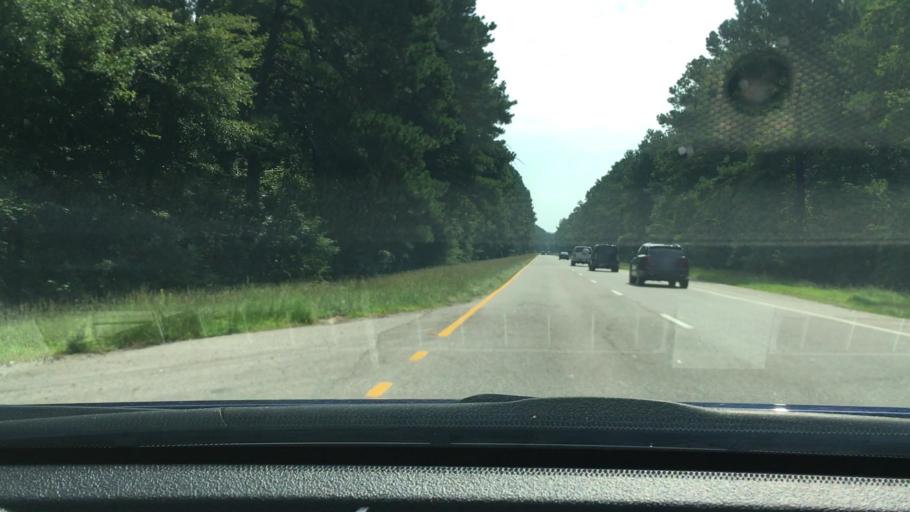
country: US
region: South Carolina
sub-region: Sumter County
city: Stateburg
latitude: 33.9519
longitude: -80.5754
